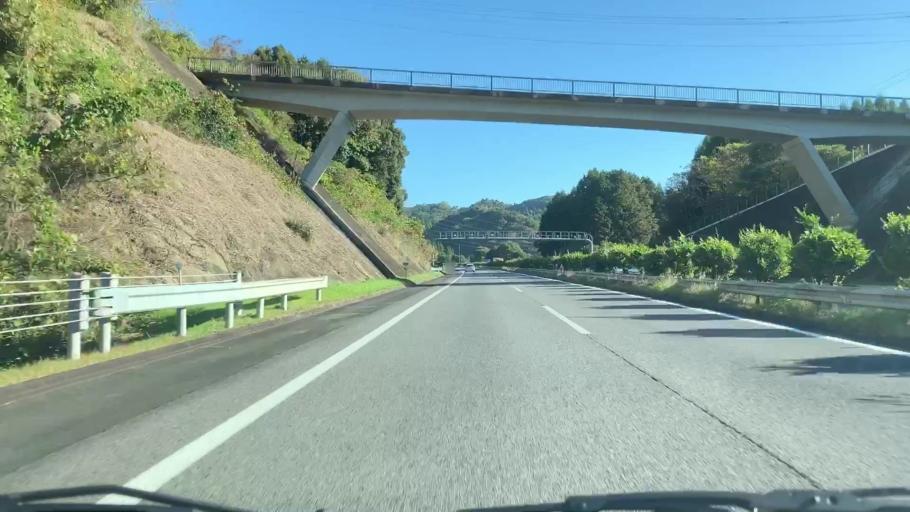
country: JP
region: Saga Prefecture
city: Takeocho-takeo
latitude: 33.2337
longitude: 130.0583
